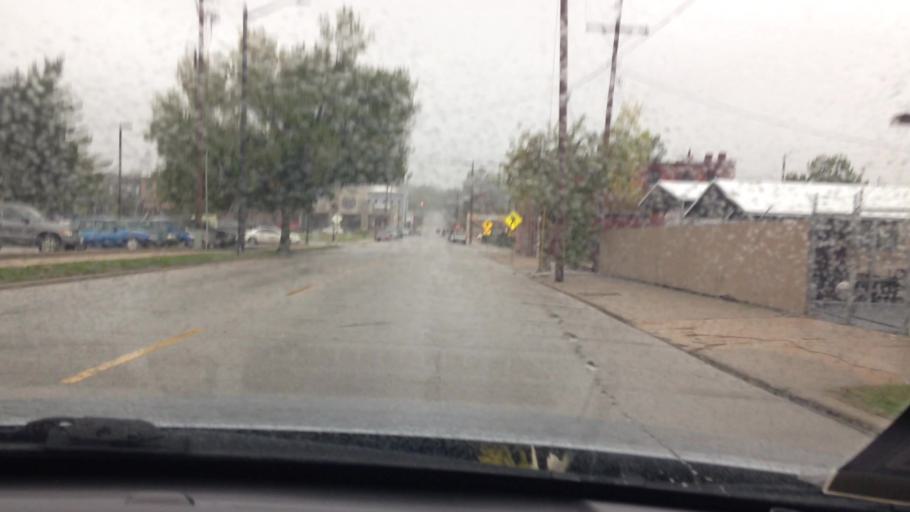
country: US
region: Kansas
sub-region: Leavenworth County
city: Leavenworth
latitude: 39.3201
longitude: -94.9126
